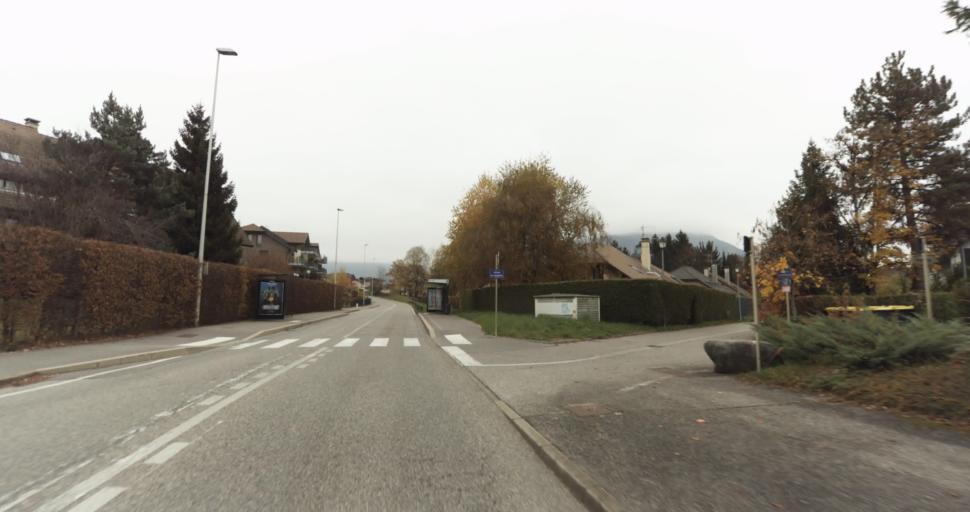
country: FR
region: Rhone-Alpes
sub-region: Departement de la Haute-Savoie
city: Annecy-le-Vieux
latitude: 45.9242
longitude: 6.1411
